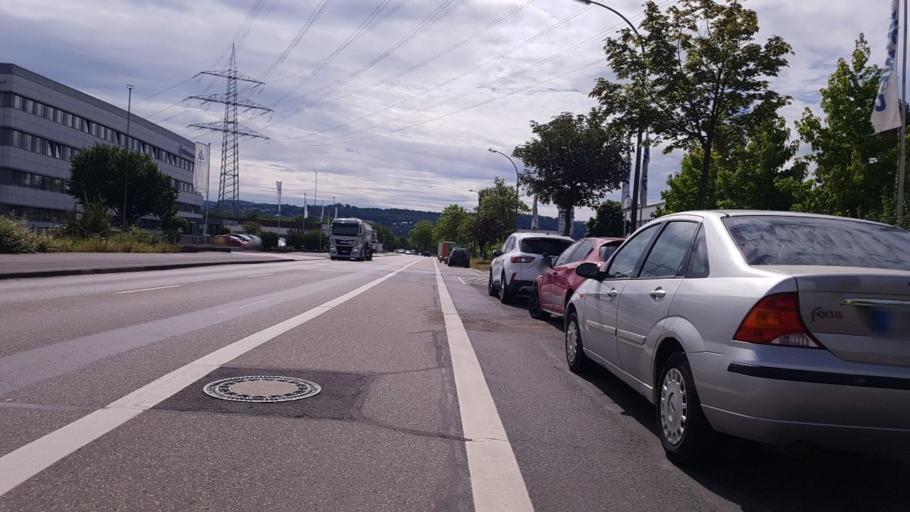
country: DE
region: Rheinland-Pfalz
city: Niederwerth
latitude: 50.3861
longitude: 7.5985
